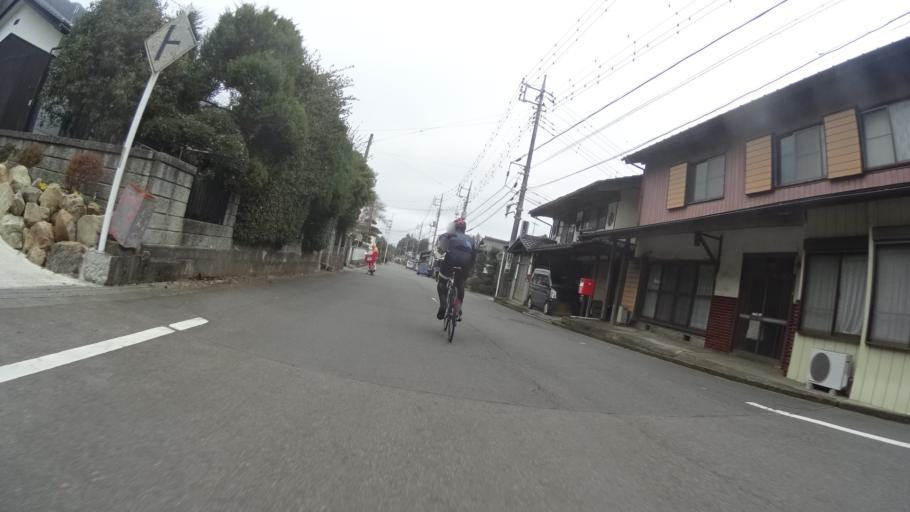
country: JP
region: Yamanashi
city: Uenohara
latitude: 35.6255
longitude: 139.0321
